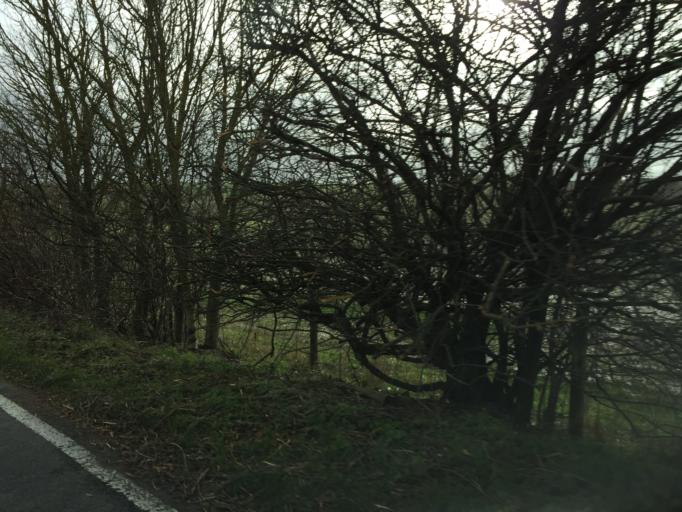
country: GB
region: England
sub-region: Oxfordshire
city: Cholsey
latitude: 51.5476
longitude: -1.1676
